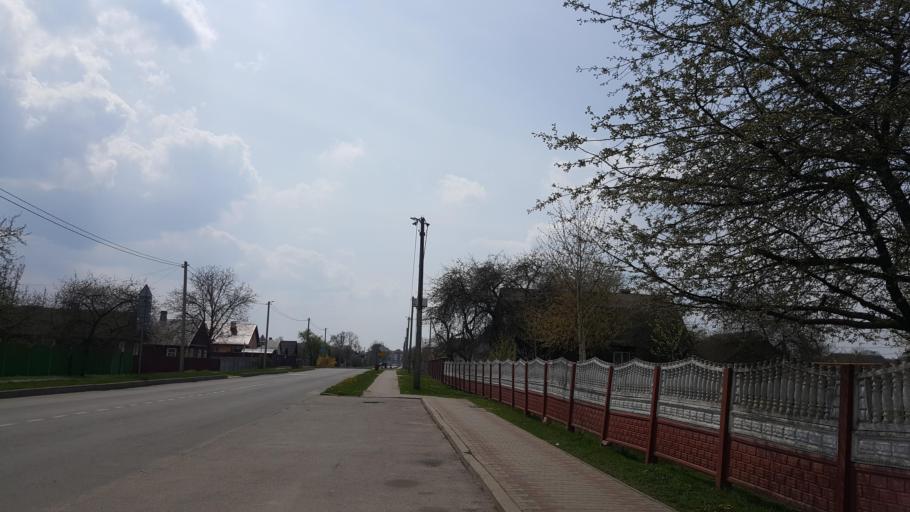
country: BY
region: Brest
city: Zhabinka
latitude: 52.2017
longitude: 24.0235
